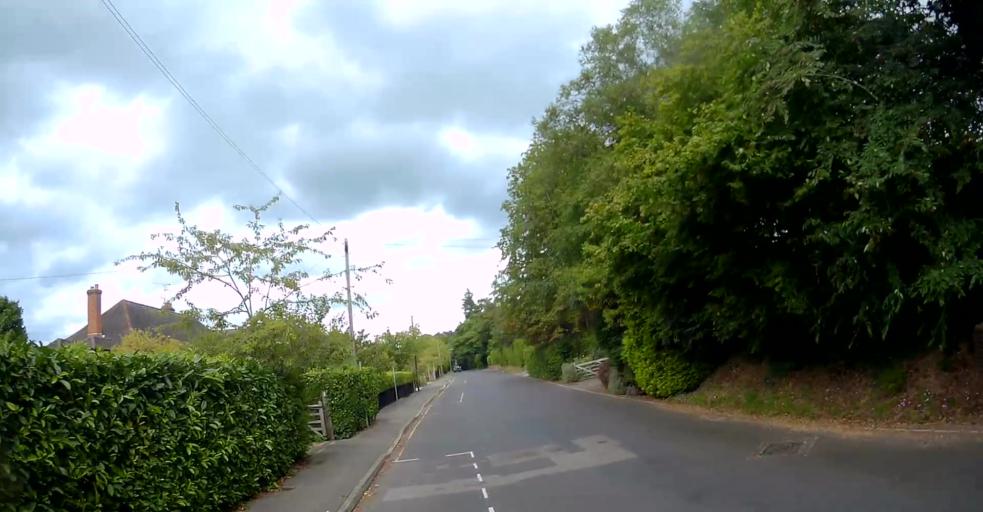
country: GB
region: England
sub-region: Surrey
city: Hale
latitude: 51.2114
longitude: -0.7804
